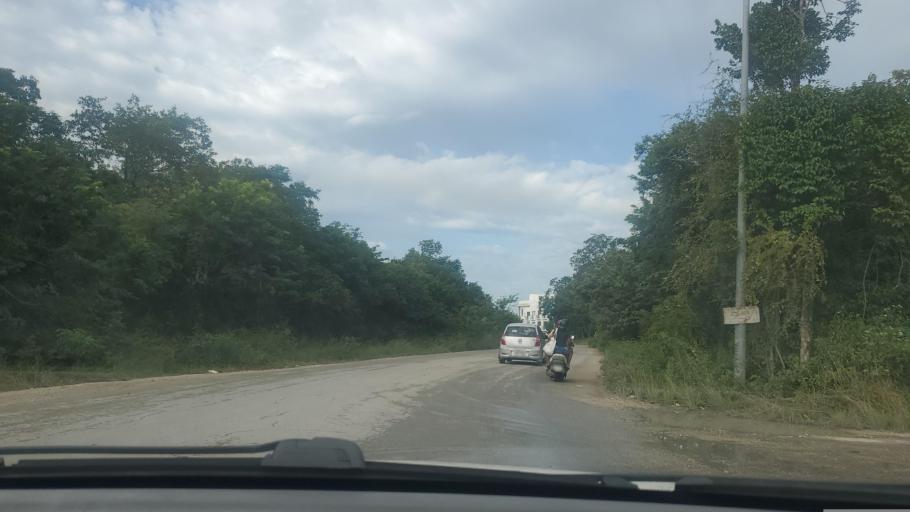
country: MX
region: Quintana Roo
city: Tulum
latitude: 20.2089
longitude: -87.4819
